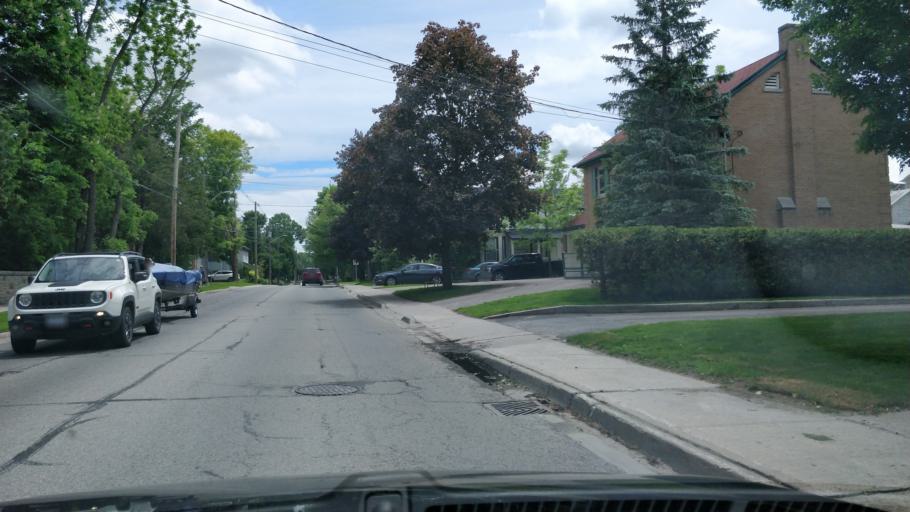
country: CA
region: Ontario
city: Perth
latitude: 44.9041
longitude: -76.2521
